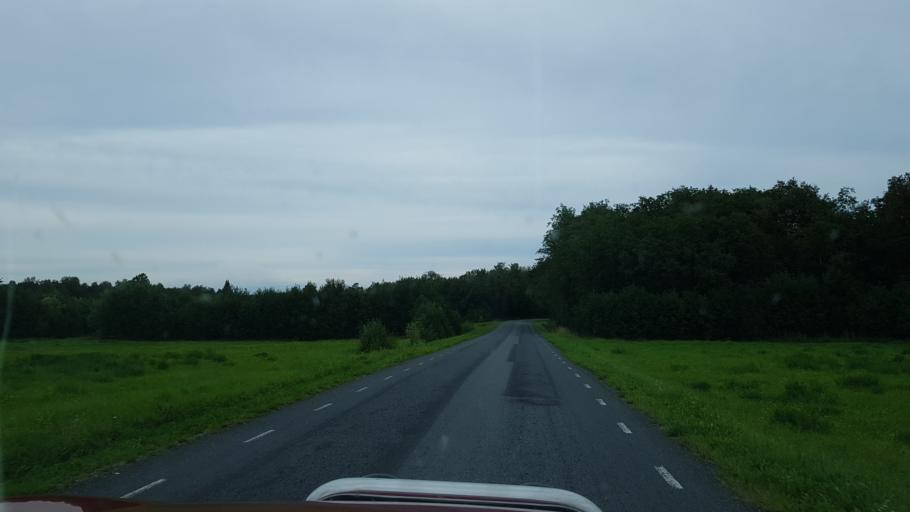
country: EE
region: Laeaene
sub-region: Lihula vald
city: Lihula
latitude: 58.8757
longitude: 23.8729
